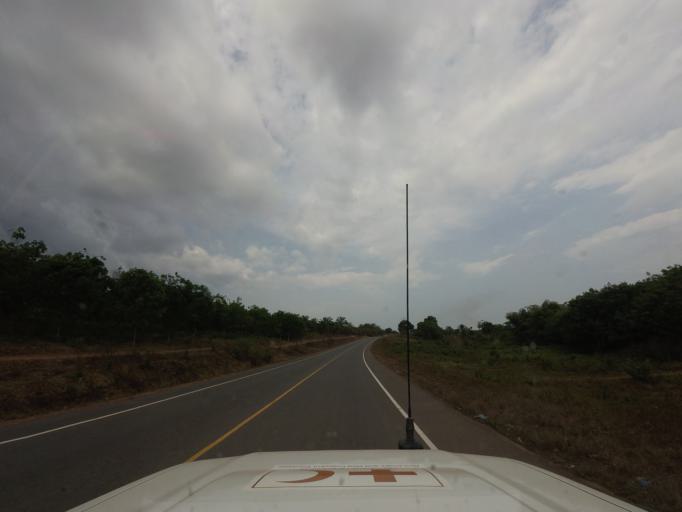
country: LR
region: Margibi
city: Kakata
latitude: 6.5789
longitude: -10.3093
